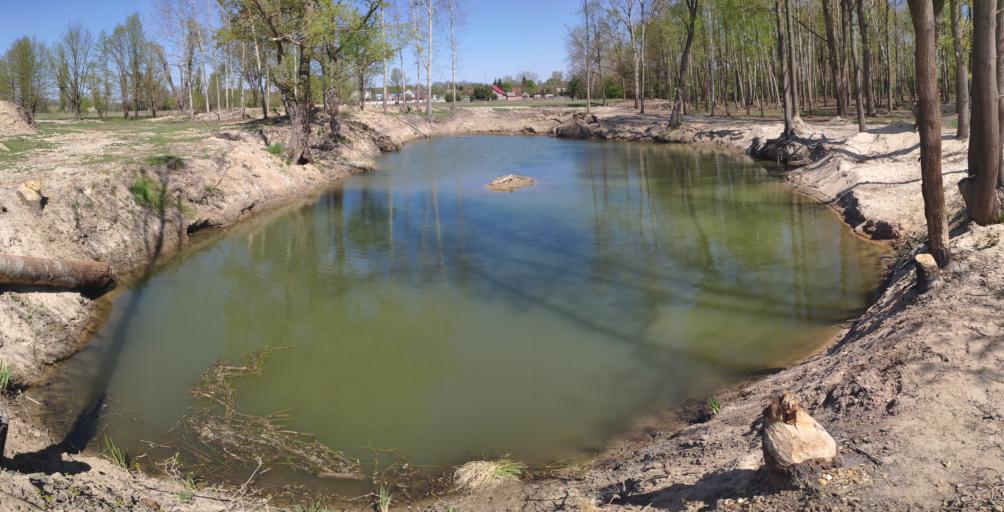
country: PL
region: Lubusz
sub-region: Powiat zielonogorski
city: Sulechow
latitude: 52.0229
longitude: 15.6162
